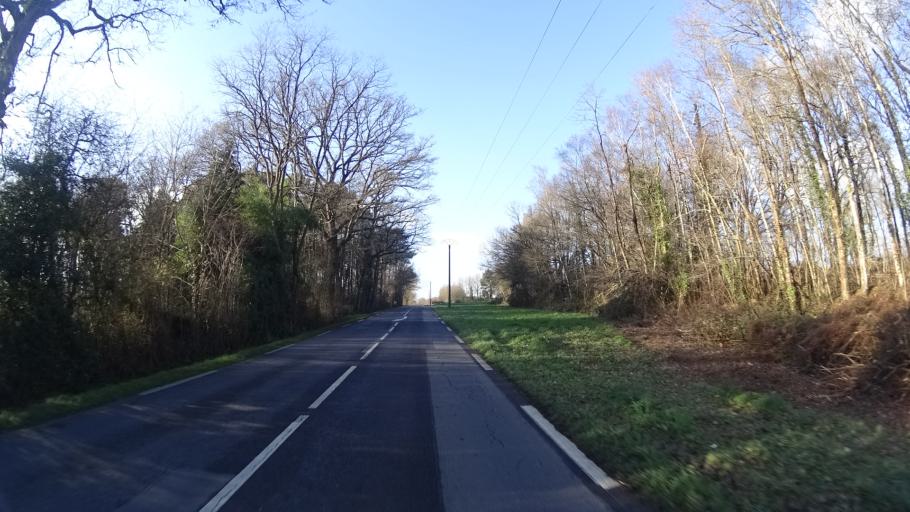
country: FR
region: Pays de la Loire
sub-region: Departement de la Loire-Atlantique
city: Plesse
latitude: 47.5328
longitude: -1.9177
